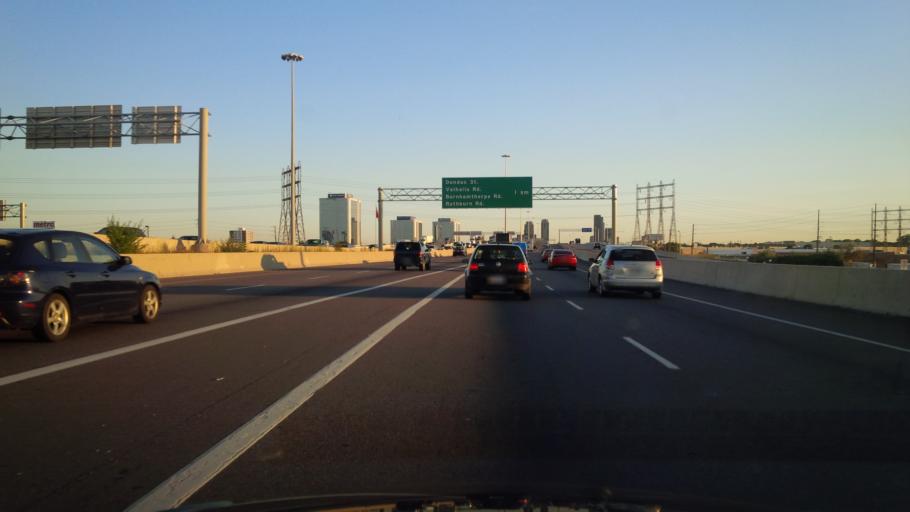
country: CA
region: Ontario
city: Etobicoke
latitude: 43.6178
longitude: -79.5519
